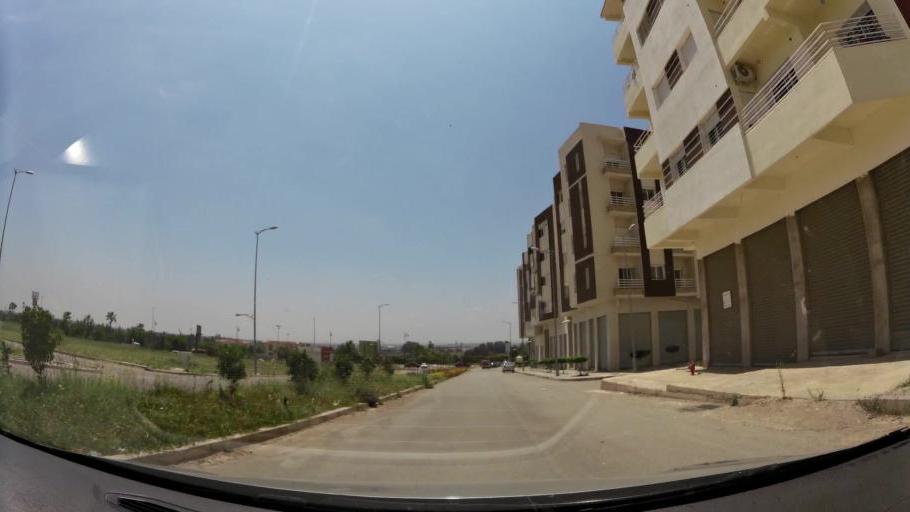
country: MA
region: Fes-Boulemane
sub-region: Fes
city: Fes
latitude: 34.0501
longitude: -5.0409
